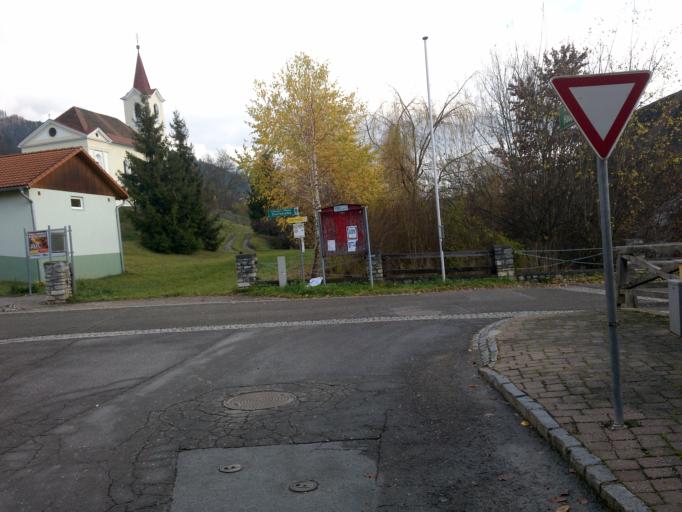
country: AT
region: Styria
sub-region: Politischer Bezirk Murtal
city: Fohnsdorf
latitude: 47.2160
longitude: 14.7012
